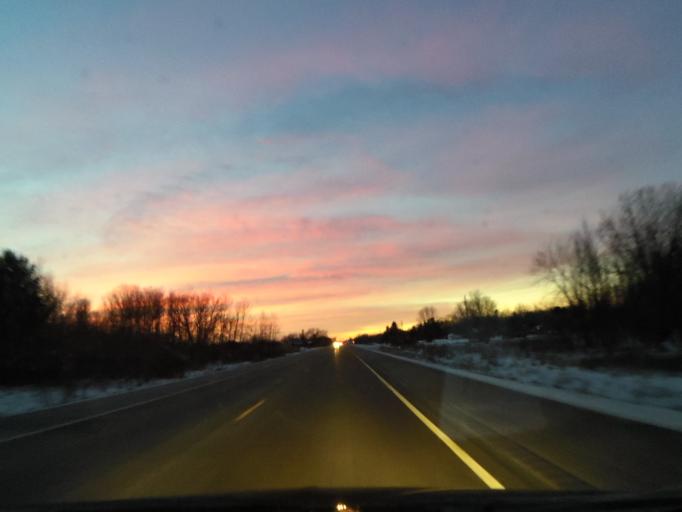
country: US
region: Minnesota
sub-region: Chisago County
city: Shafer
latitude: 45.3828
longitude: -92.7315
